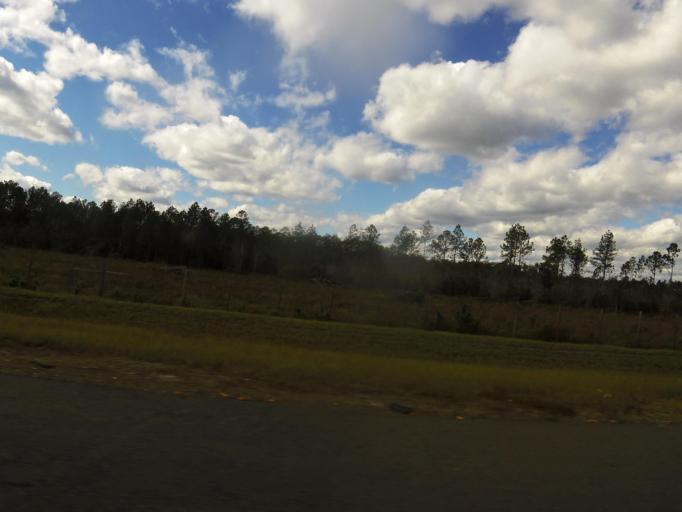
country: US
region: Florida
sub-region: Bradford County
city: Starke
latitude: 29.9522
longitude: -82.1375
